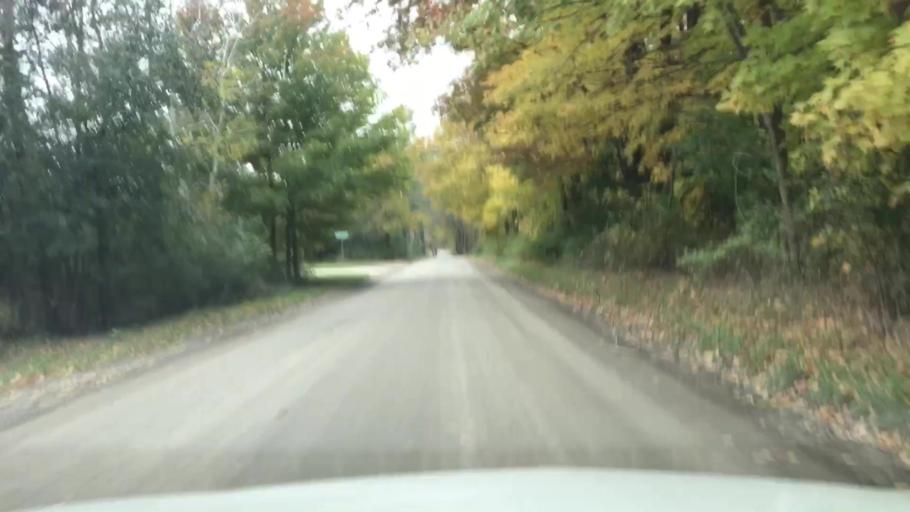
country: US
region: Michigan
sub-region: Oakland County
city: Rochester
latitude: 42.7135
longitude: -83.1252
